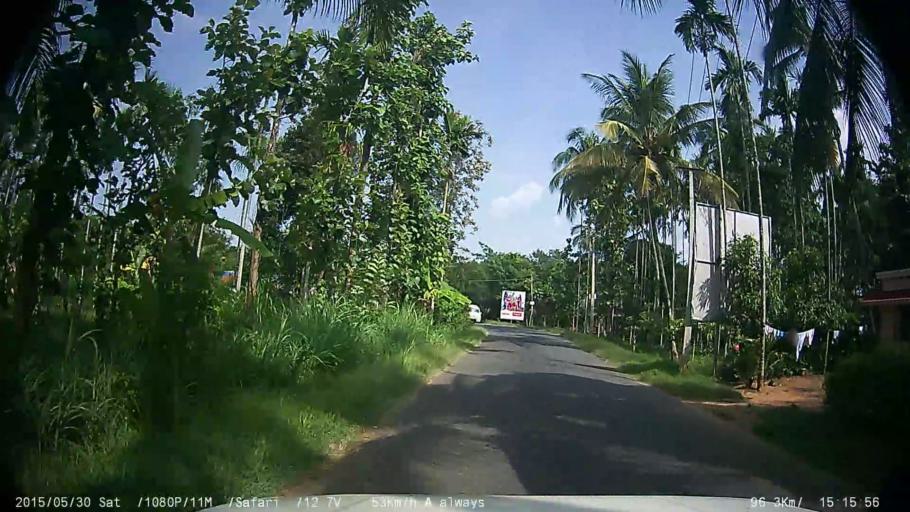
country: IN
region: Kerala
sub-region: Wayanad
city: Panamaram
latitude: 11.7773
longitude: 76.0518
